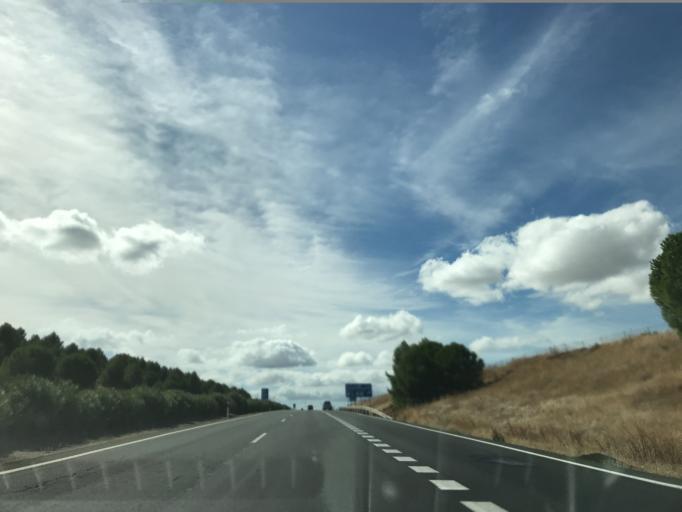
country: ES
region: Andalusia
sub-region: Province of Cordoba
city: La Victoria
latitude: 37.7232
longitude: -4.8598
